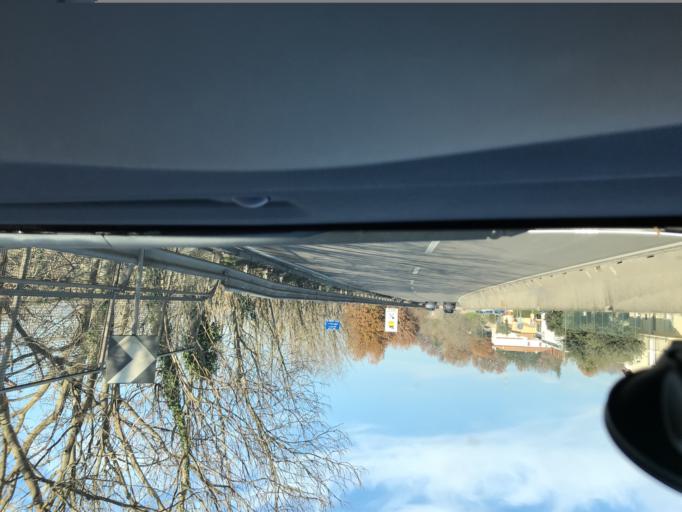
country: IT
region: Latium
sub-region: Provincia di Viterbo
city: Orte Scalo
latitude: 42.4541
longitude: 12.4107
